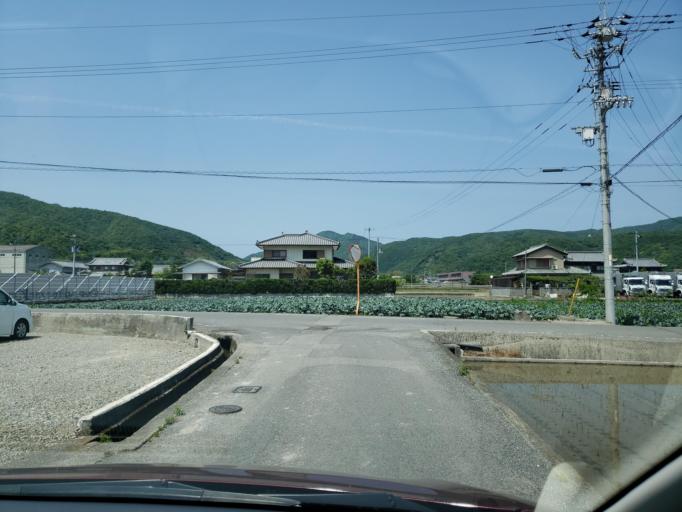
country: JP
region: Tokushima
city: Kamojimacho-jogejima
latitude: 34.0988
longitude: 134.2690
